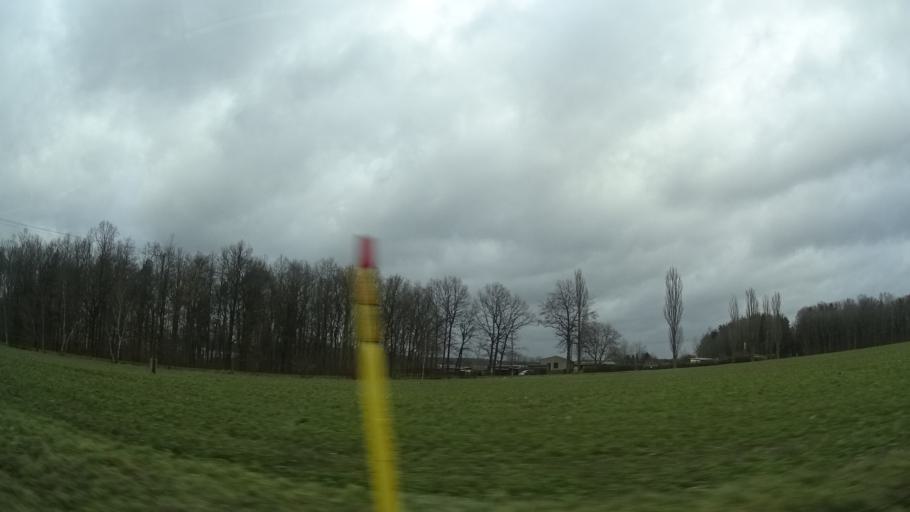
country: DE
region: Thuringia
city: Zeulenroda
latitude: 50.6366
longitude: 11.9884
